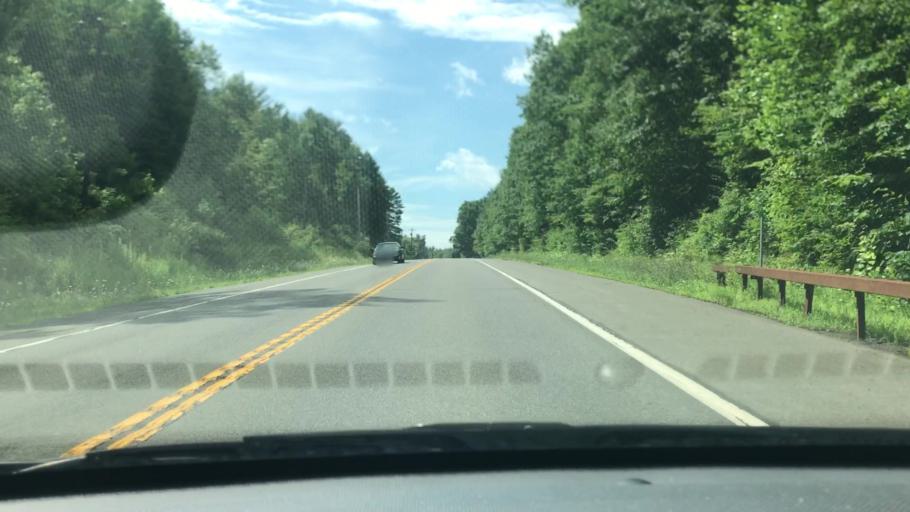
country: US
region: New York
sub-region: Ulster County
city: Shokan
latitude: 42.0020
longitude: -74.2650
